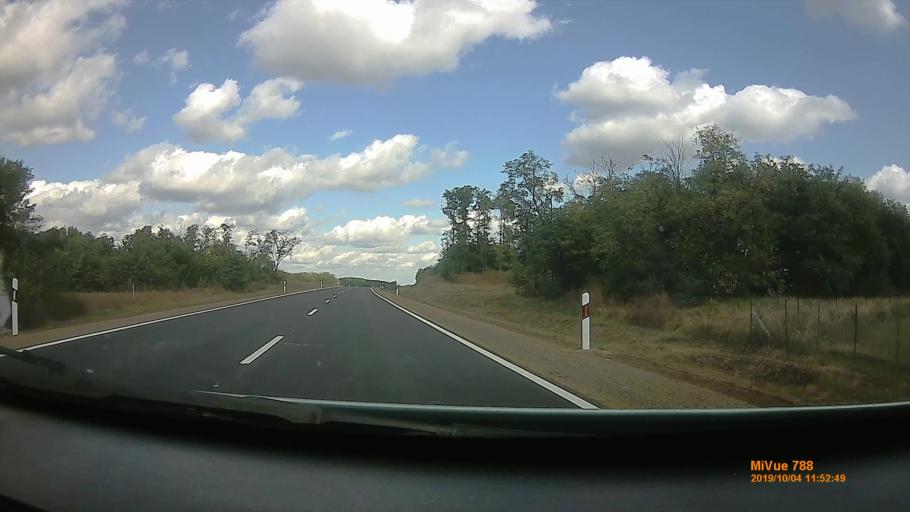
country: HU
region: Szabolcs-Szatmar-Bereg
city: Nyirtelek
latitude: 48.0025
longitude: 21.6731
